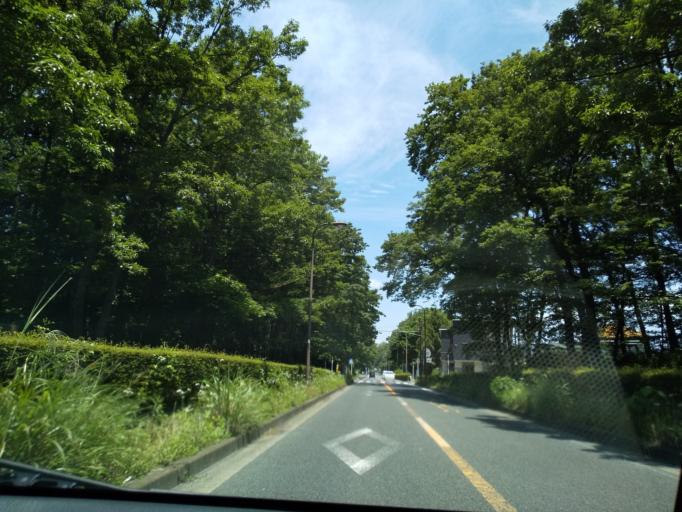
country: JP
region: Tokyo
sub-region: Machida-shi
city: Machida
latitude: 35.5399
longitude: 139.4122
